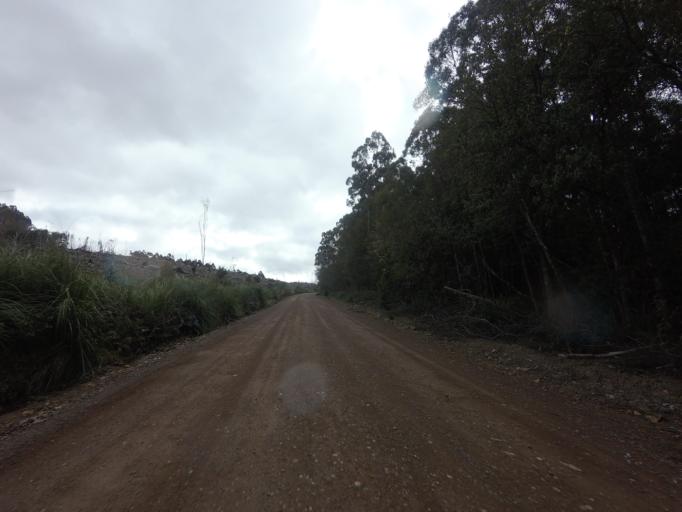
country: AU
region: Tasmania
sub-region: Huon Valley
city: Geeveston
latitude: -43.4899
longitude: 146.8877
